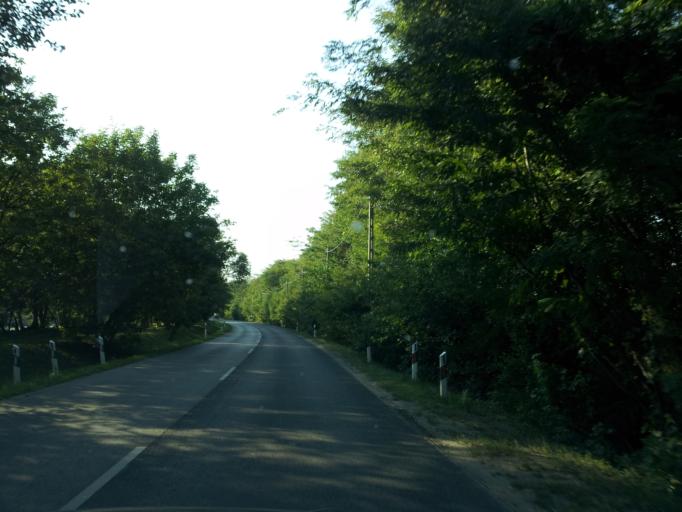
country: HU
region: Pest
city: Tahitotfalu
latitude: 47.7621
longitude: 19.0696
